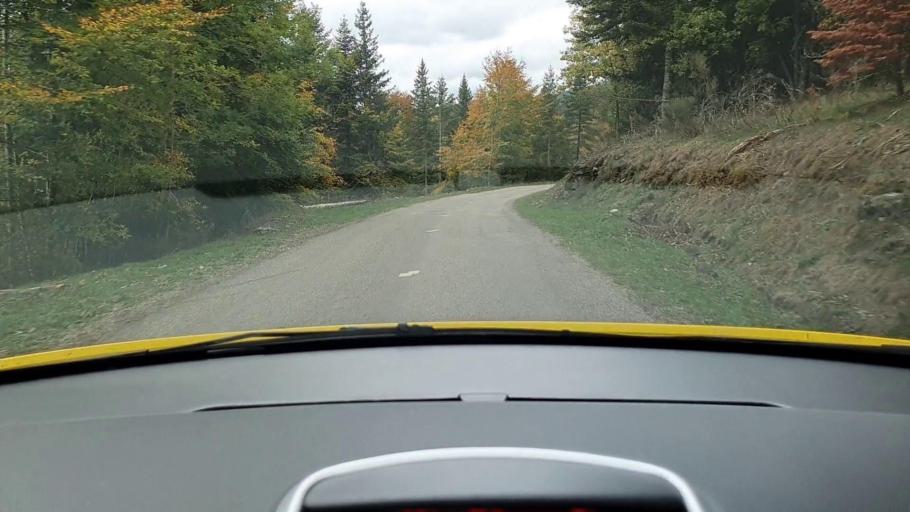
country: FR
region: Languedoc-Roussillon
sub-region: Departement de la Lozere
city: Meyrueis
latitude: 44.1070
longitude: 3.4826
